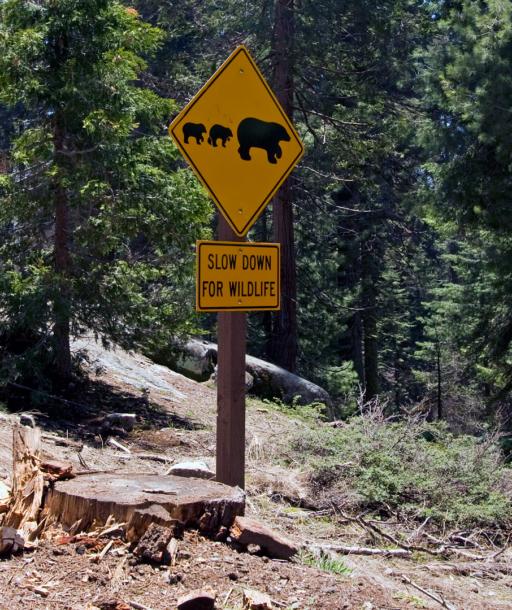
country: US
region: California
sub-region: Tulare County
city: Three Rivers
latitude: 36.5632
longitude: -118.7736
